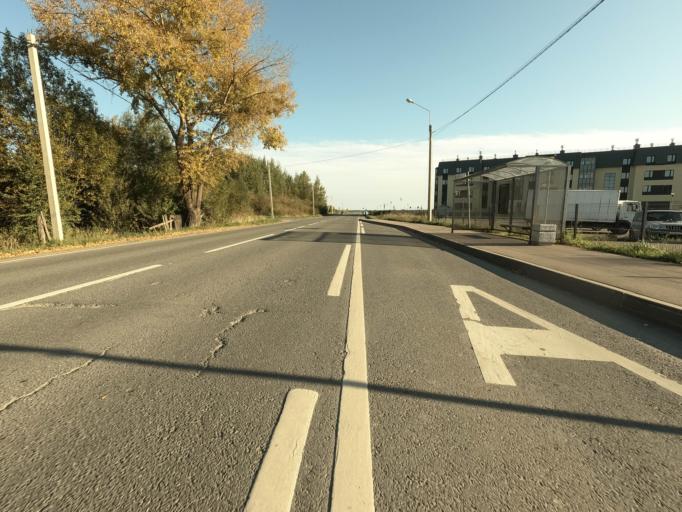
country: RU
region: St.-Petersburg
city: Pontonnyy
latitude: 59.7560
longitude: 30.6303
